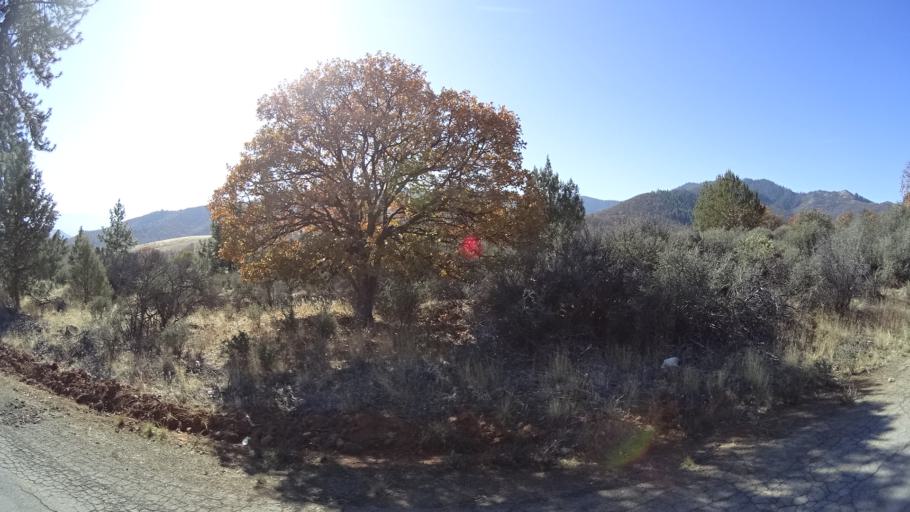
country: US
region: California
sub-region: Siskiyou County
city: Yreka
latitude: 41.7725
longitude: -122.6359
